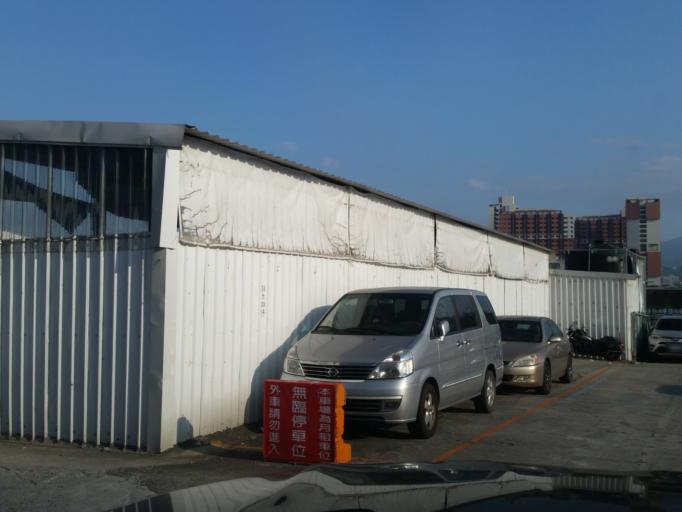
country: TW
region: Taipei
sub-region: Taipei
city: Banqiao
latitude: 24.9852
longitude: 121.5215
